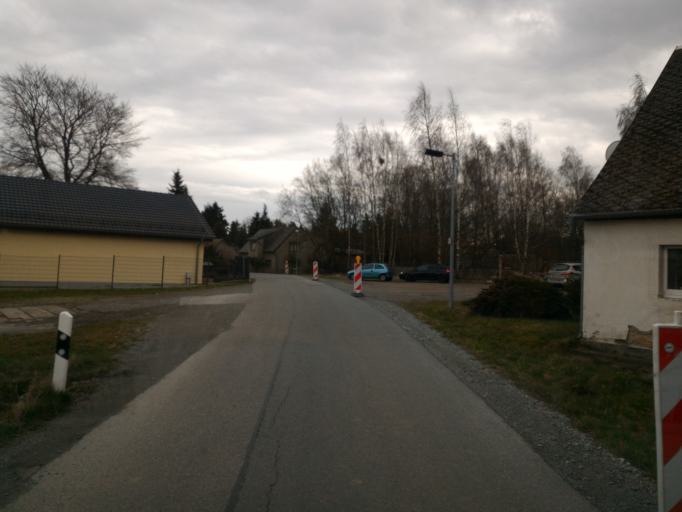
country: DE
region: Saxony
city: Ebersbach
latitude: 51.0032
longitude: 14.6076
